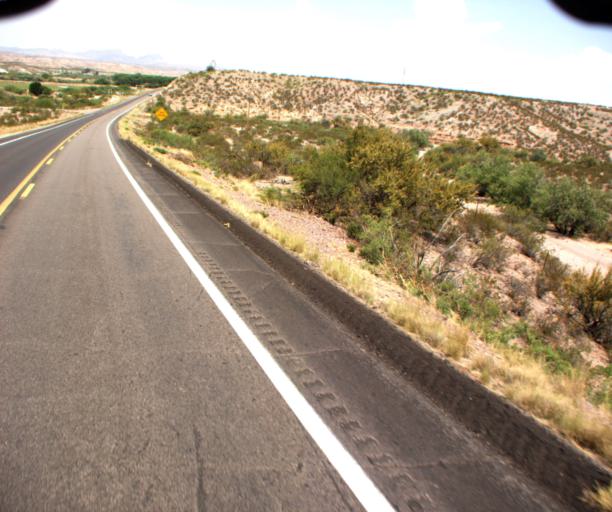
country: US
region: Arizona
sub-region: Greenlee County
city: Clifton
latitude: 32.7400
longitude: -109.1391
